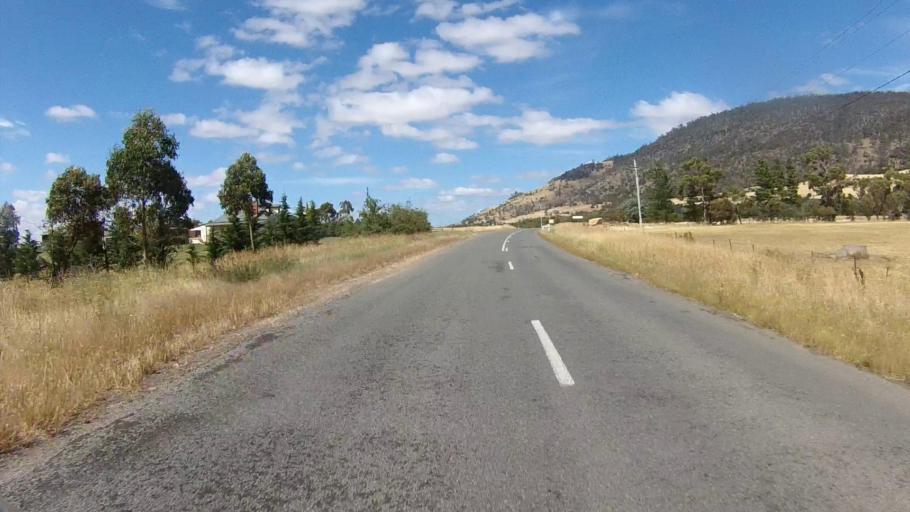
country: AU
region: Tasmania
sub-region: Sorell
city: Sorell
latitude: -42.6220
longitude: 147.4296
